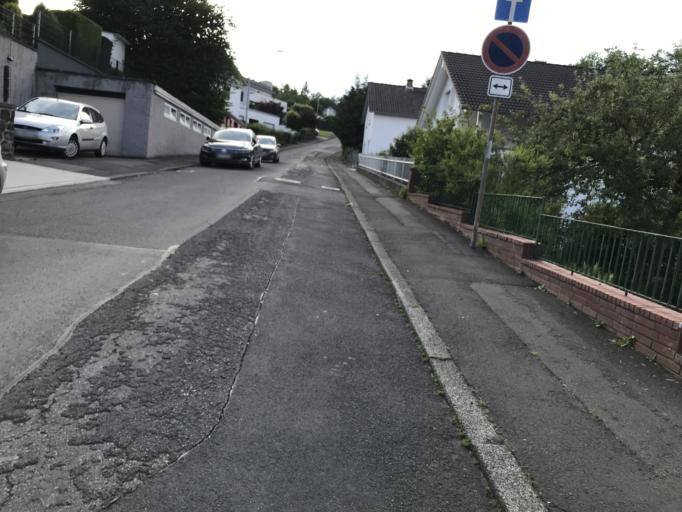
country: DE
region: Hesse
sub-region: Regierungsbezirk Giessen
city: Lich
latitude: 50.5122
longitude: 8.8171
